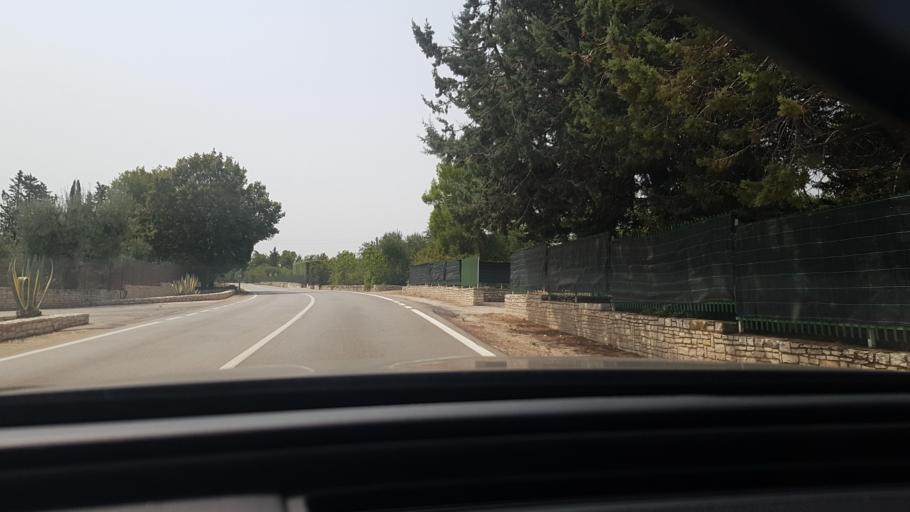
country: IT
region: Apulia
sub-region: Provincia di Barletta - Andria - Trani
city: Andria
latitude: 41.1311
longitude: 16.2905
